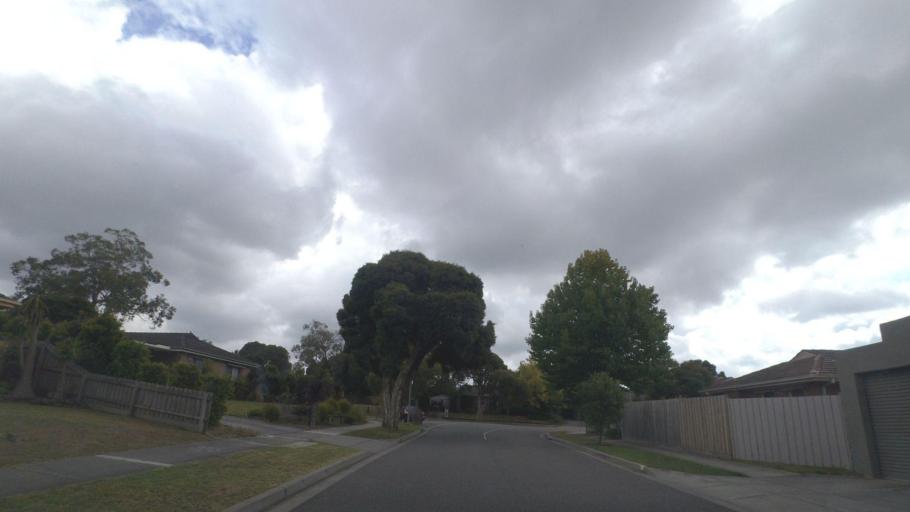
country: AU
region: Victoria
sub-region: Knox
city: Scoresby
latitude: -37.8938
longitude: 145.2243
